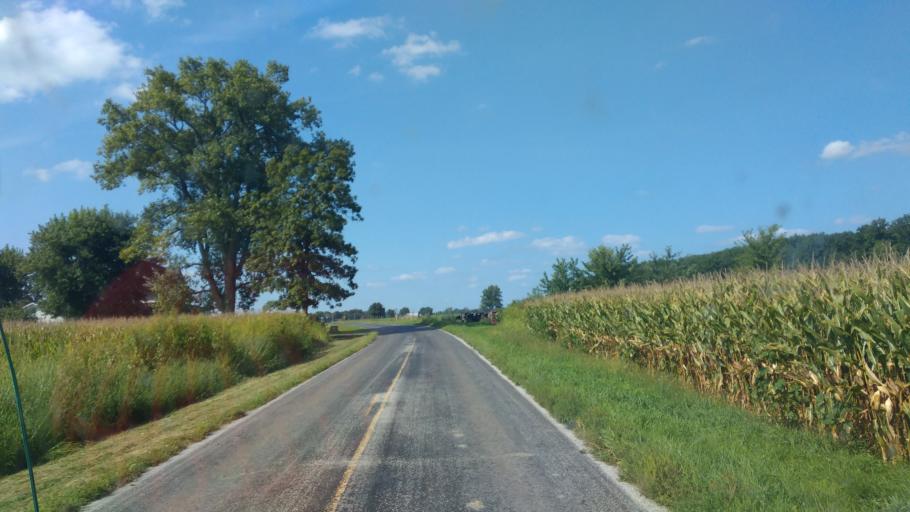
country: US
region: Ohio
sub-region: Hardin County
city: Kenton
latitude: 40.5970
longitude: -83.4647
